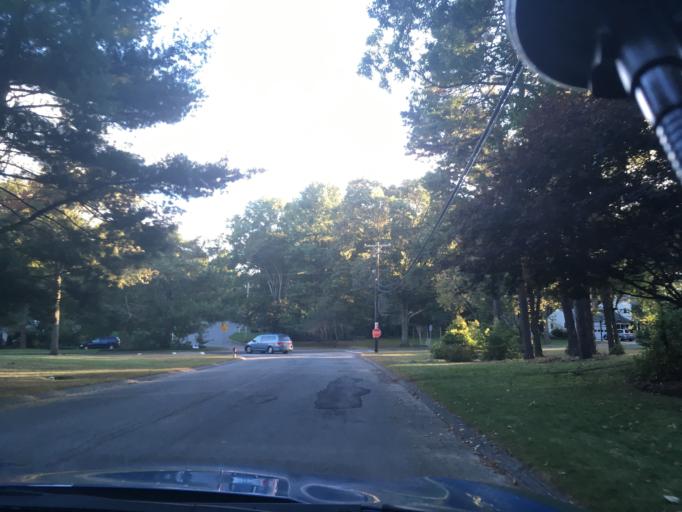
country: US
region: Rhode Island
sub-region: Kent County
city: East Greenwich
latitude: 41.6390
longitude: -71.4766
